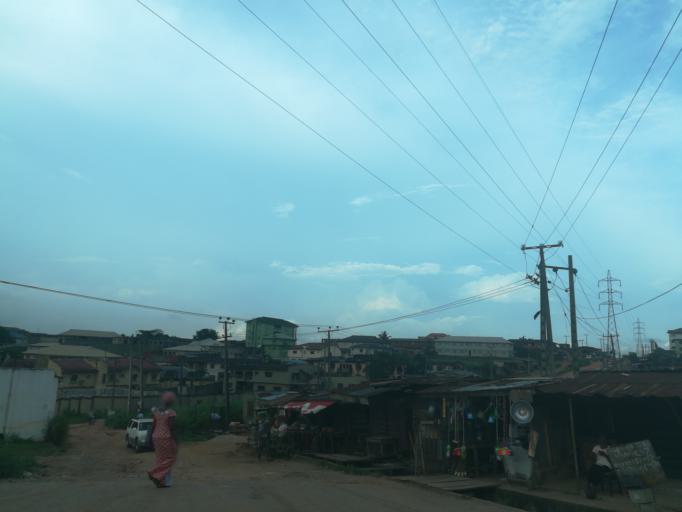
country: NG
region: Lagos
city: Ikorodu
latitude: 6.6259
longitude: 3.4943
